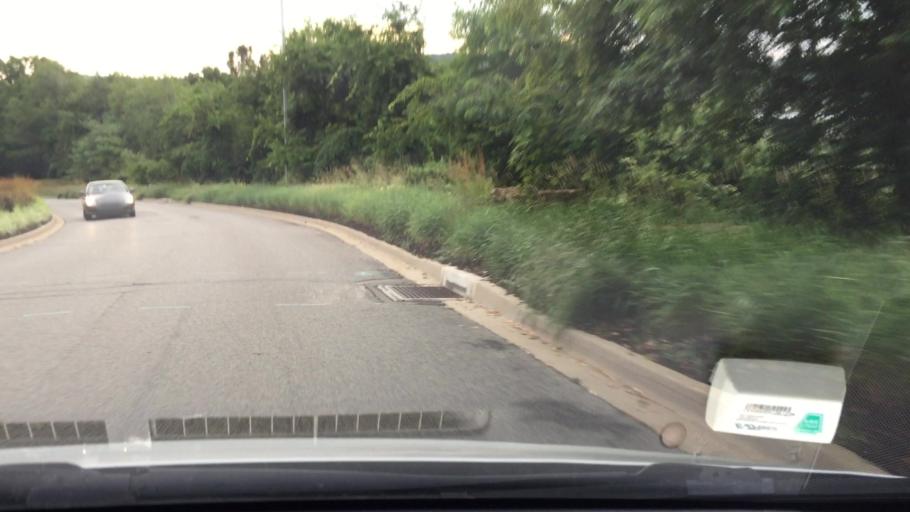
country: US
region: Pennsylvania
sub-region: Allegheny County
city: Bradford Woods
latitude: 40.6588
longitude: -80.0987
